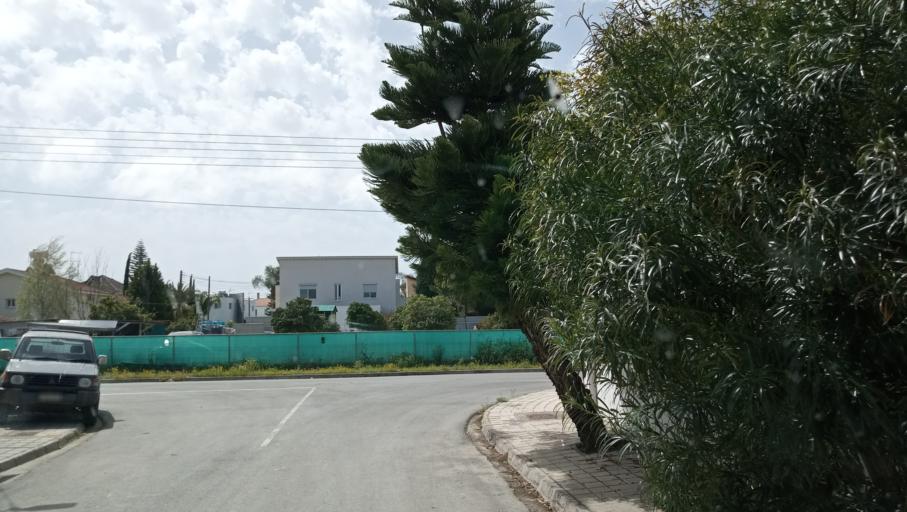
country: CY
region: Lefkosia
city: Dali
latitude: 35.0236
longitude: 33.4266
